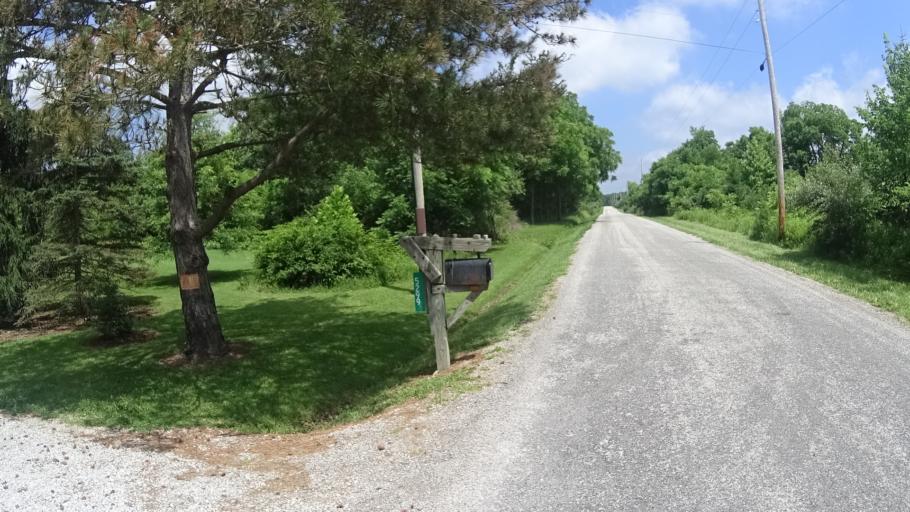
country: US
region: Ohio
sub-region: Lorain County
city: Camden
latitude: 41.2806
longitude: -82.3423
